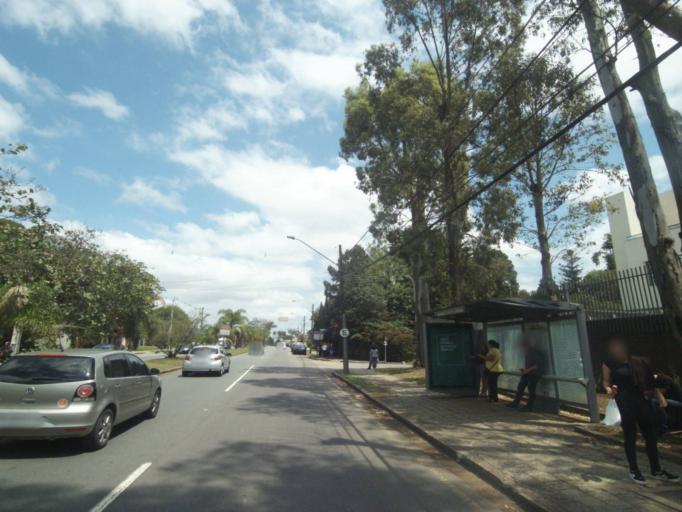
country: BR
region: Parana
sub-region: Curitiba
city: Curitiba
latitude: -25.4151
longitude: -49.2415
